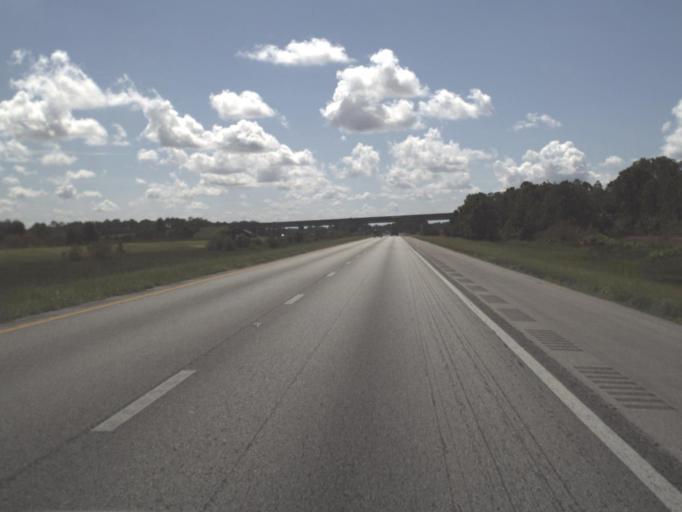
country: US
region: Florida
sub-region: Lee County
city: Suncoast Estates
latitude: 26.8134
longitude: -81.9353
